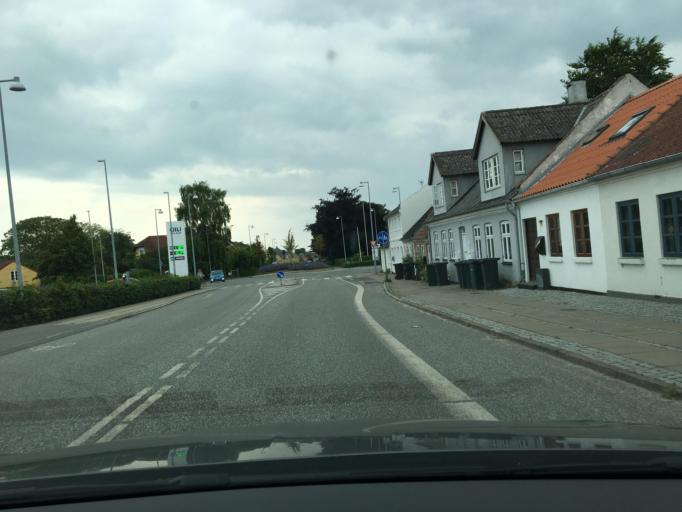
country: DK
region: South Denmark
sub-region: Assens Kommune
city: Assens
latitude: 55.2741
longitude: 9.9072
